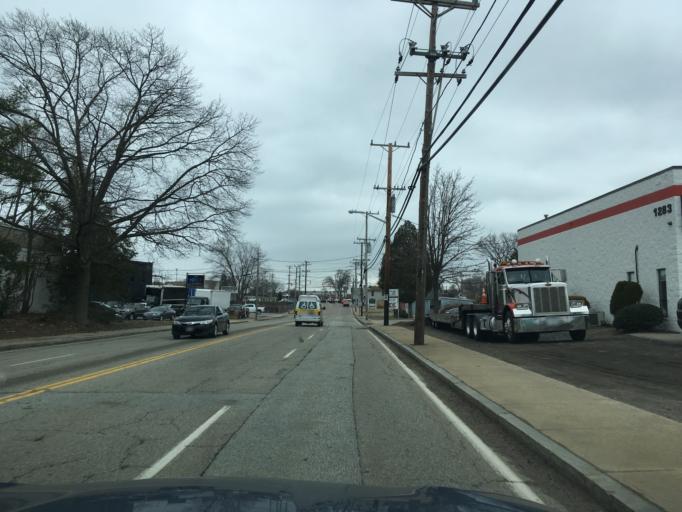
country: US
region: Rhode Island
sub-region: Kent County
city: Warwick
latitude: 41.7138
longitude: -71.4482
